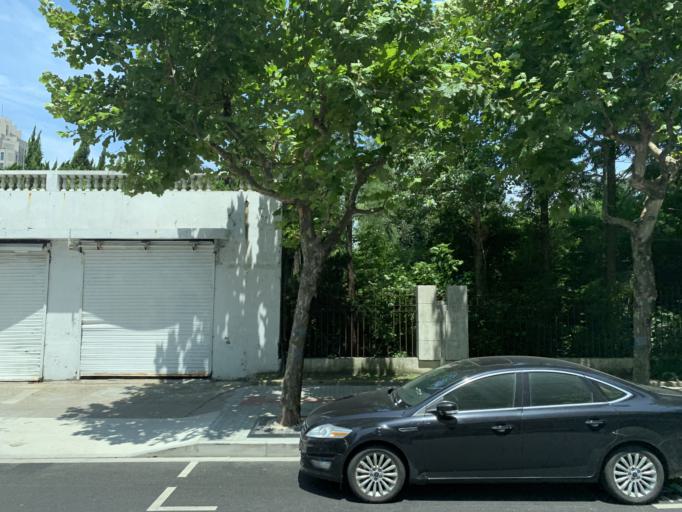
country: CN
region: Shanghai Shi
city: Pudong
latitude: 31.2472
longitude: 121.5644
